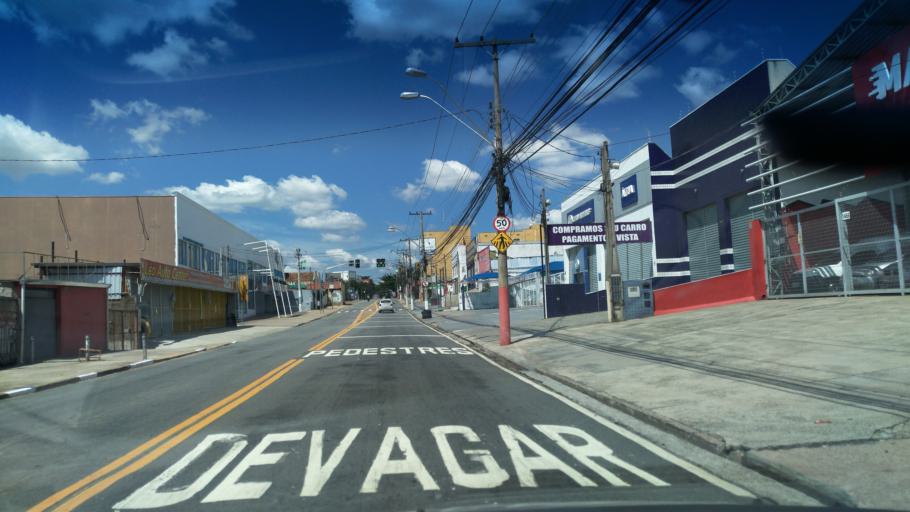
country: BR
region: Sao Paulo
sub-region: Campinas
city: Campinas
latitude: -22.9240
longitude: -47.0462
